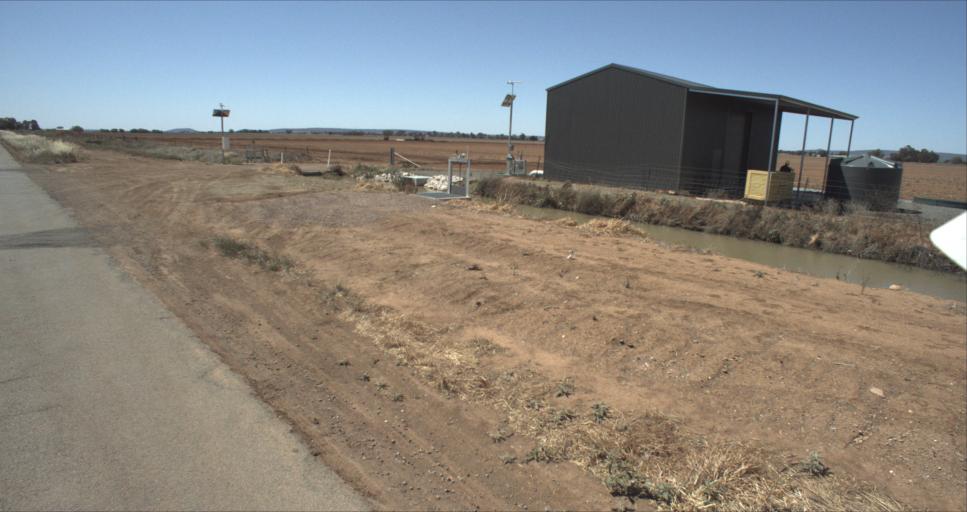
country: AU
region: New South Wales
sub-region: Leeton
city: Leeton
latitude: -34.5222
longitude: 146.3457
